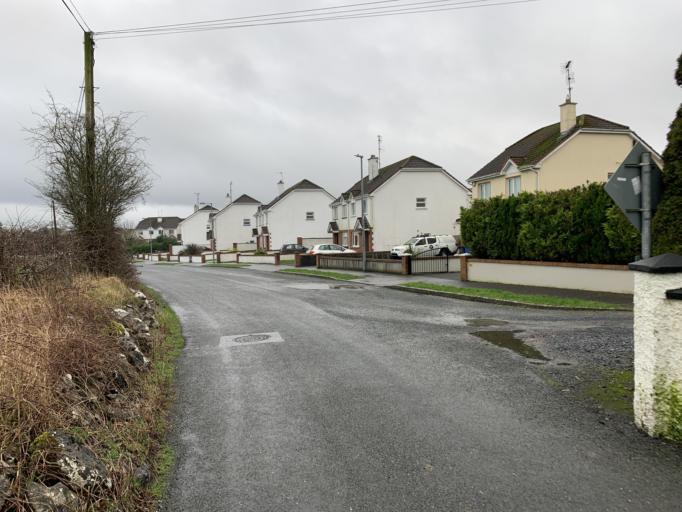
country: IE
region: Connaught
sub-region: County Galway
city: Tuam
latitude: 53.5124
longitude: -8.8697
